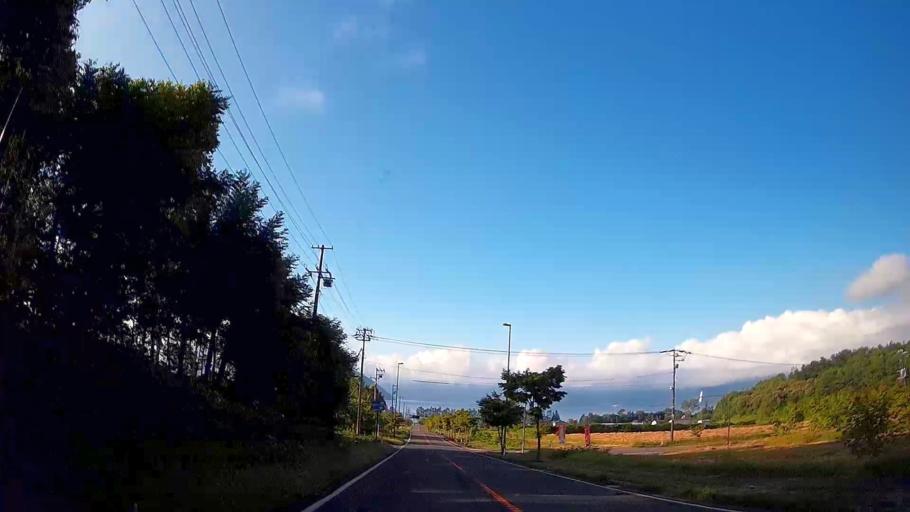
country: JP
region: Hokkaido
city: Date
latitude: 42.5523
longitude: 140.8621
